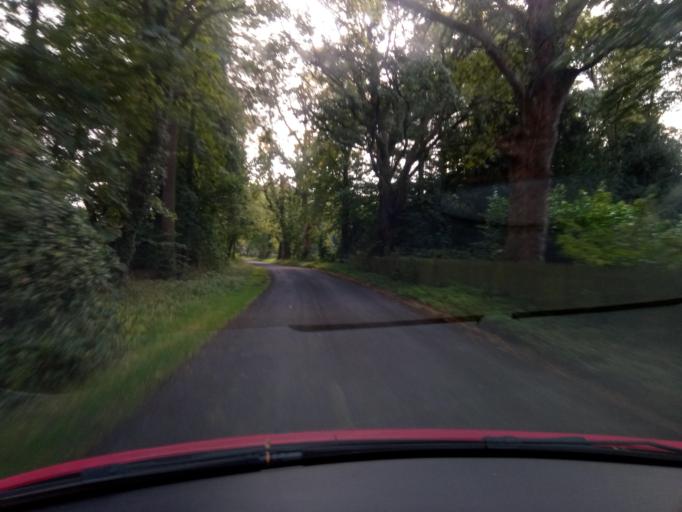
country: GB
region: Scotland
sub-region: The Scottish Borders
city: Kelso
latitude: 55.5090
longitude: -2.3513
